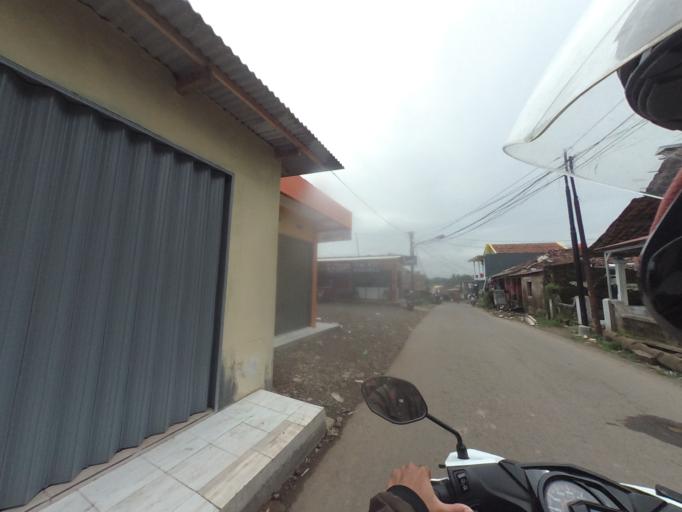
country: ID
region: West Java
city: Bogor
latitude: -6.6376
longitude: 106.7493
